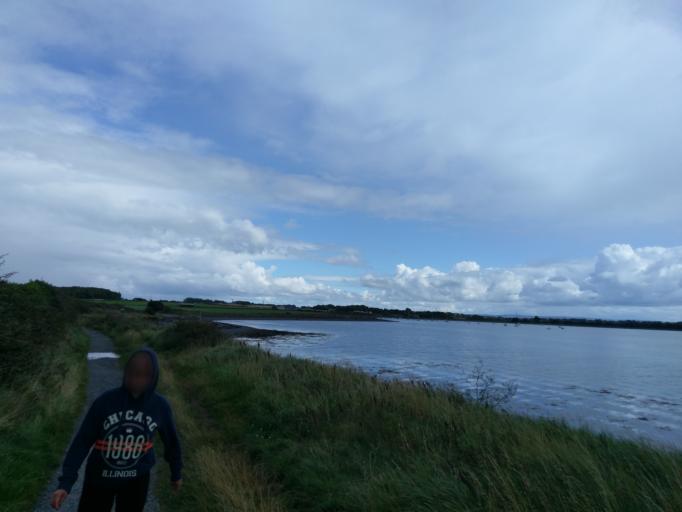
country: IE
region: Connaught
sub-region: County Galway
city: Oranmore
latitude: 53.2450
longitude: -8.9783
